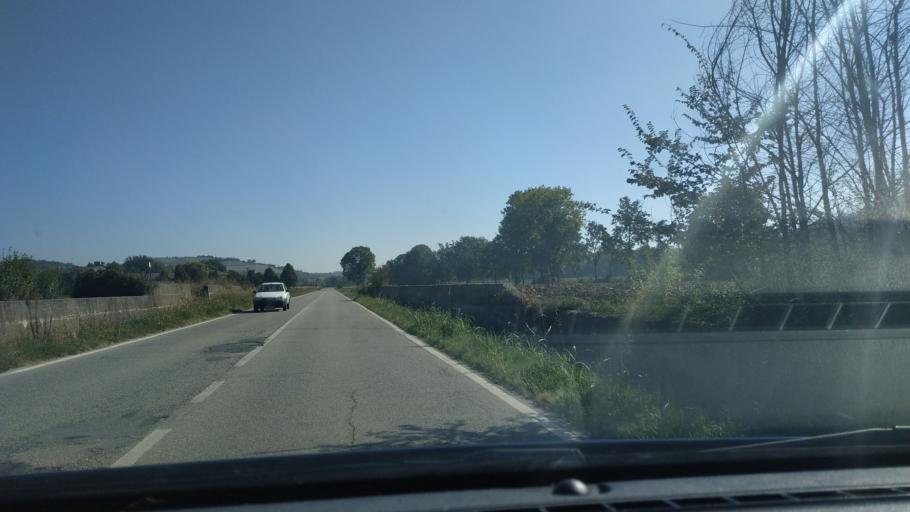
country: IT
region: Piedmont
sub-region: Provincia di Alessandria
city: Cerrina
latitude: 45.1178
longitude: 8.2276
